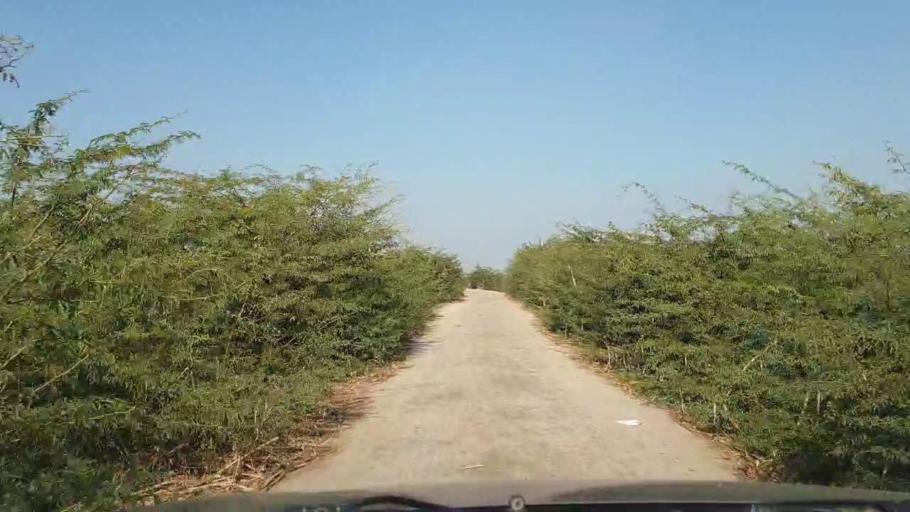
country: PK
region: Sindh
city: Jhol
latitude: 25.9065
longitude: 68.8305
